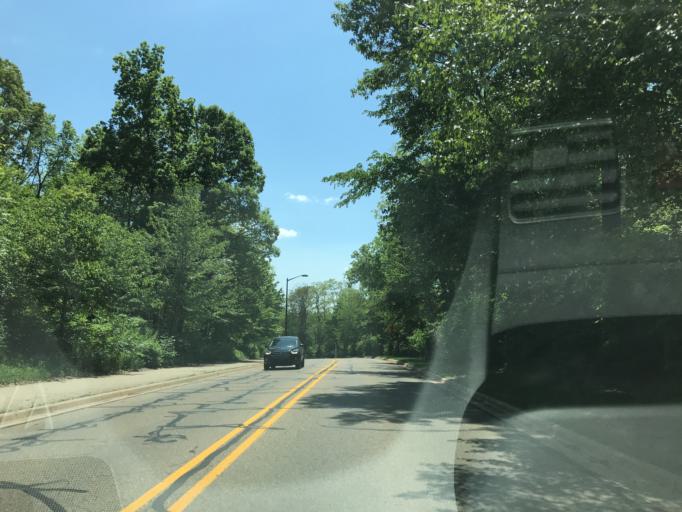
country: US
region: Michigan
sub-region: Washtenaw County
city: Ann Arbor
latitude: 42.2852
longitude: -83.7111
